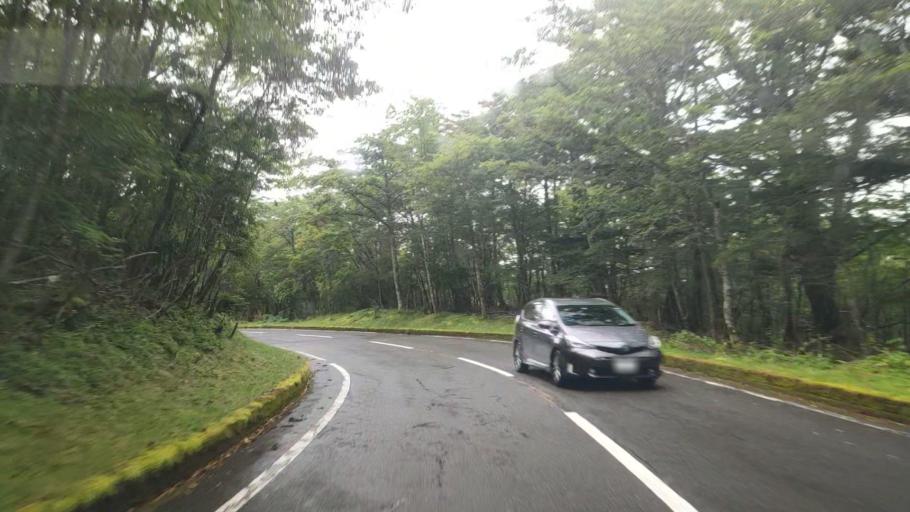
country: JP
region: Shizuoka
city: Fuji
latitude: 35.3082
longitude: 138.7432
